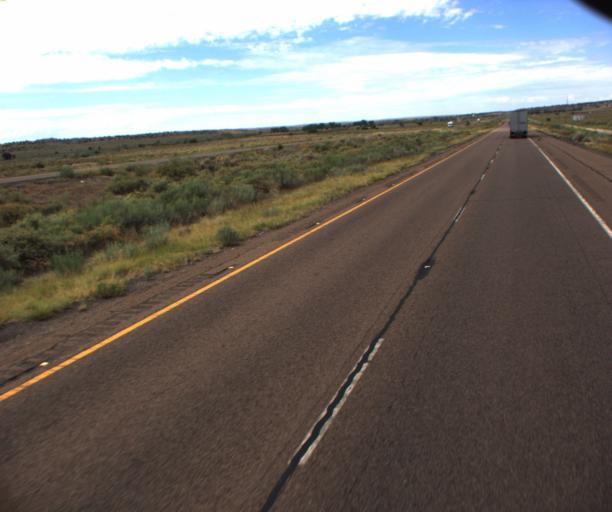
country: US
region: Arizona
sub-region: Apache County
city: Houck
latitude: 35.1791
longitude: -109.4639
